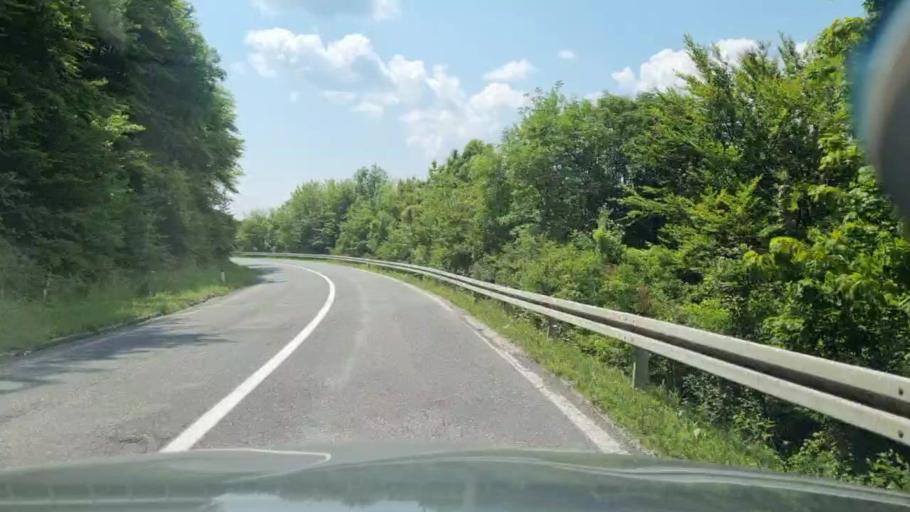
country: BA
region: Federation of Bosnia and Herzegovina
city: Tojsici
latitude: 44.5405
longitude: 18.8445
